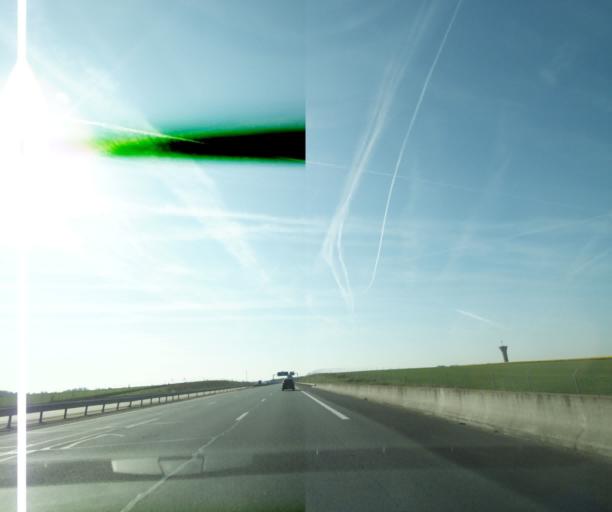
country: FR
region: Ile-de-France
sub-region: Departement de Seine-et-Marne
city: Souppes-sur-Loing
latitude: 48.2297
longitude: 2.7595
